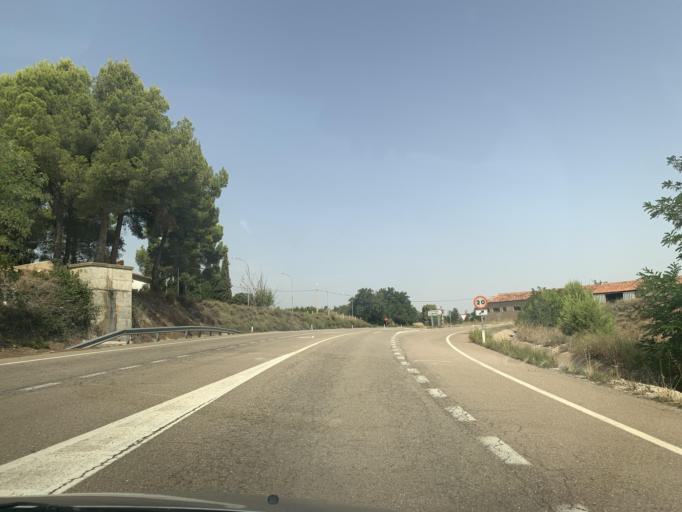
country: ES
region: Aragon
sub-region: Provincia de Zaragoza
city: Belchite
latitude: 41.2990
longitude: -0.7432
